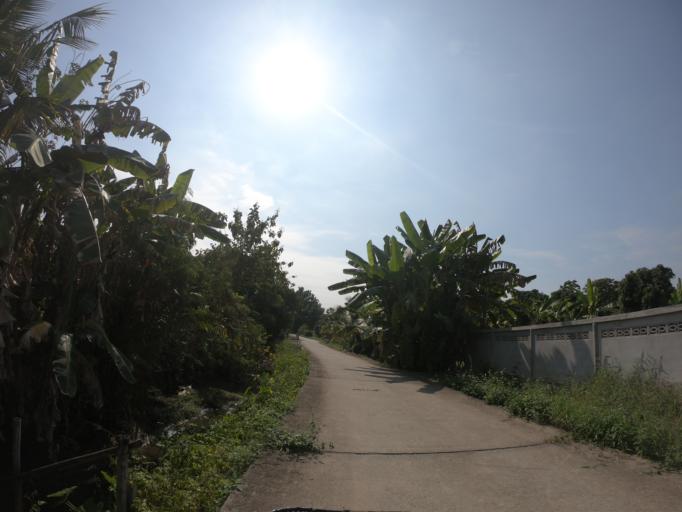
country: TH
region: Chiang Mai
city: Saraphi
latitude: 18.6957
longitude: 99.0579
